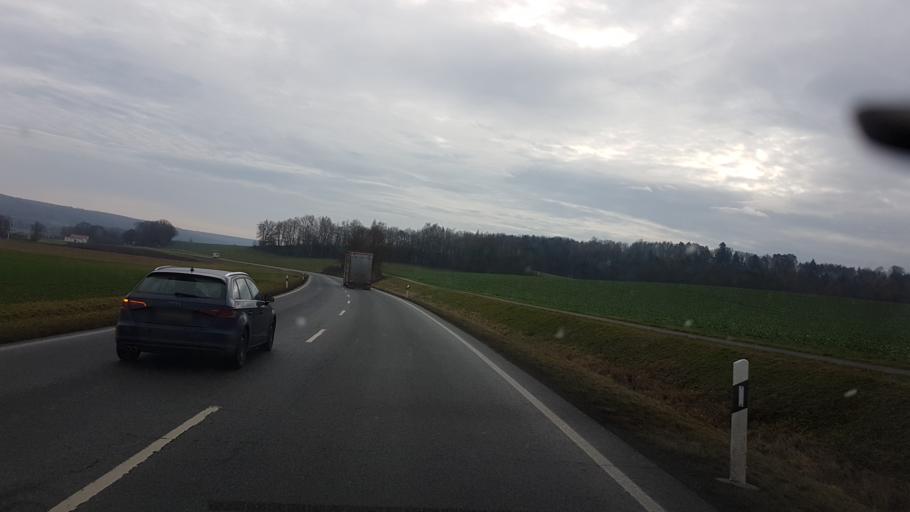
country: DE
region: Bavaria
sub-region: Upper Franconia
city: Gerach
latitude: 50.0451
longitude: 10.8126
